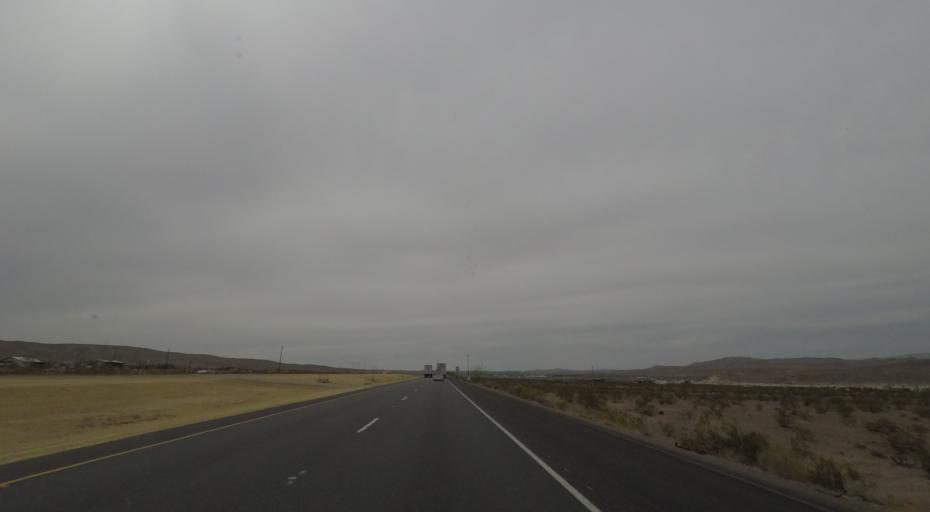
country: US
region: California
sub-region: San Bernardino County
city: Barstow
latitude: 34.8573
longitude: -116.9005
